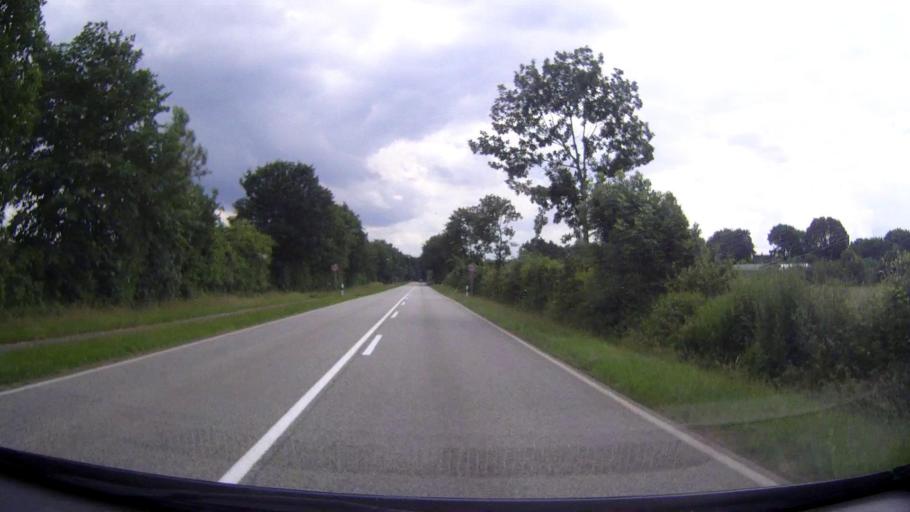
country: DE
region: Schleswig-Holstein
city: Warringholz
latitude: 54.0850
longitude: 9.4649
